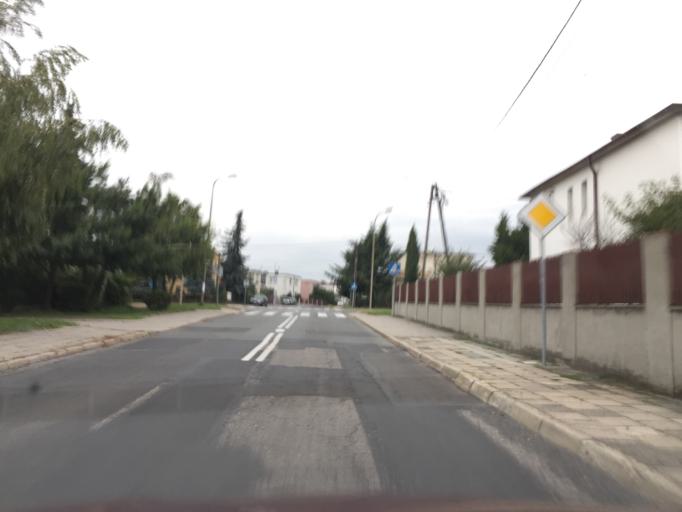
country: PL
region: Greater Poland Voivodeship
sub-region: Kalisz
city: Kalisz
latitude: 51.7780
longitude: 18.0847
